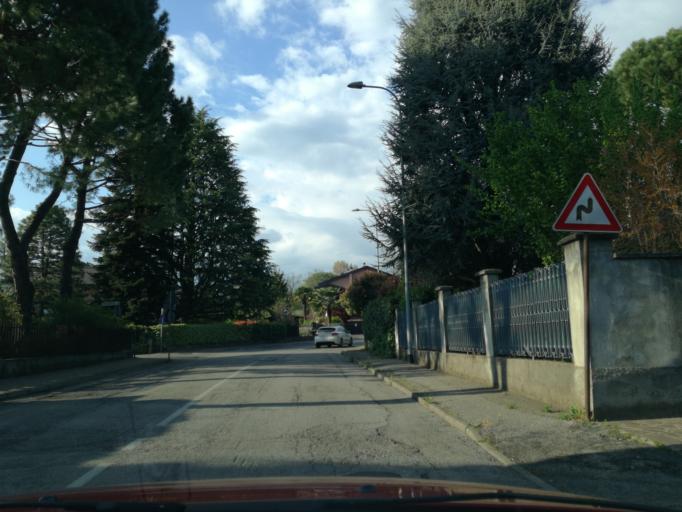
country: IT
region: Lombardy
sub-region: Provincia di Monza e Brianza
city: Carnate
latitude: 45.6426
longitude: 9.3758
